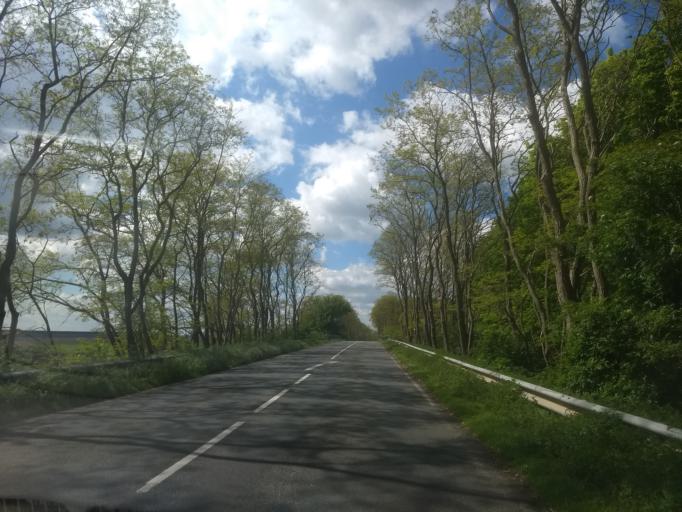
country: FR
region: Nord-Pas-de-Calais
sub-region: Departement du Pas-de-Calais
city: Bailleul-Sir-Berthoult
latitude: 50.3289
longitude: 2.8294
